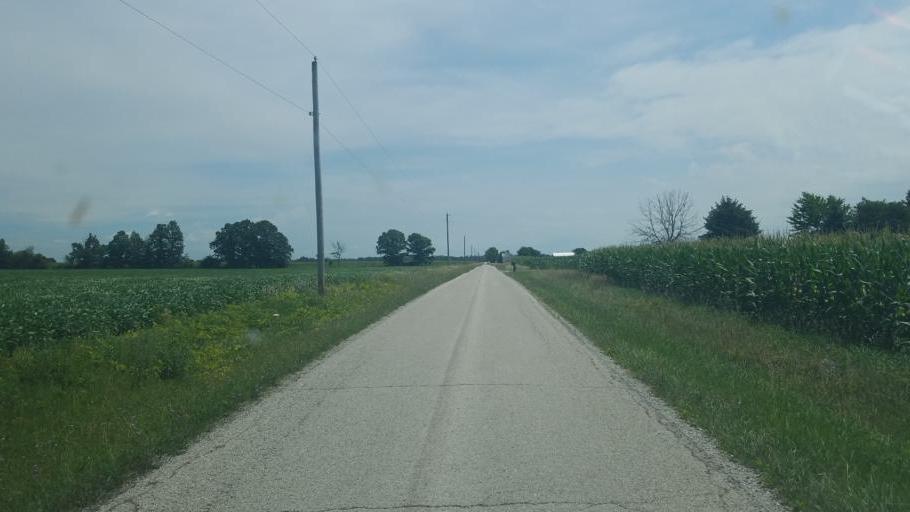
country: US
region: Ohio
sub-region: Crawford County
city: Bucyrus
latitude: 40.8776
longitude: -82.9768
